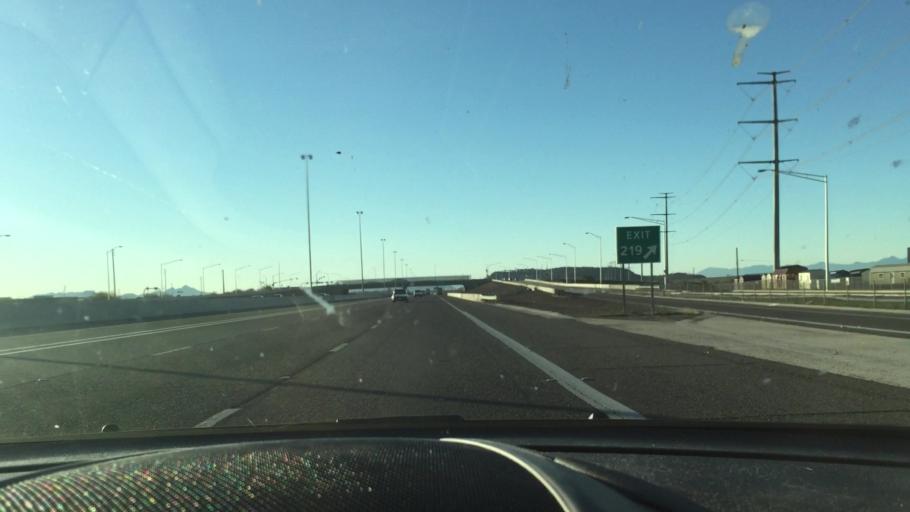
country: US
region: Arizona
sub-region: Maricopa County
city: Anthem
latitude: 33.7305
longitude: -112.1198
